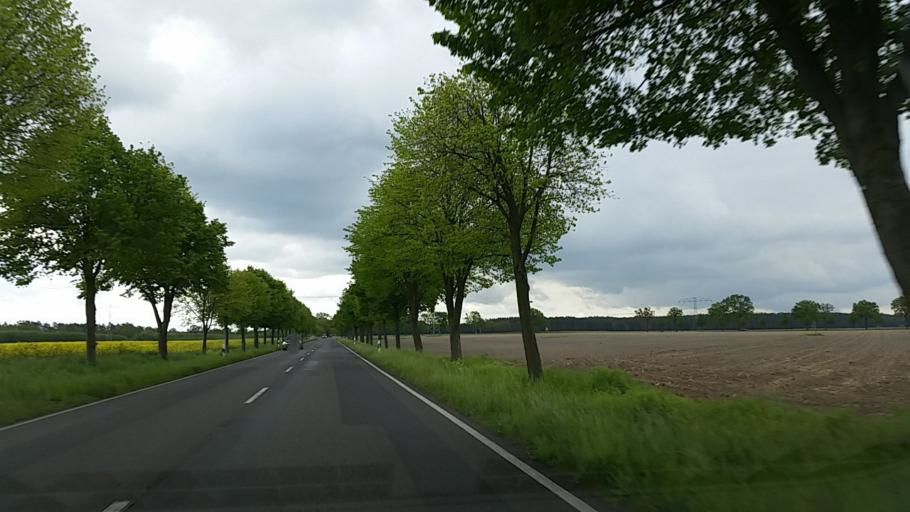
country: DE
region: Brandenburg
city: Storkow
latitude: 52.2776
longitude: 13.9086
